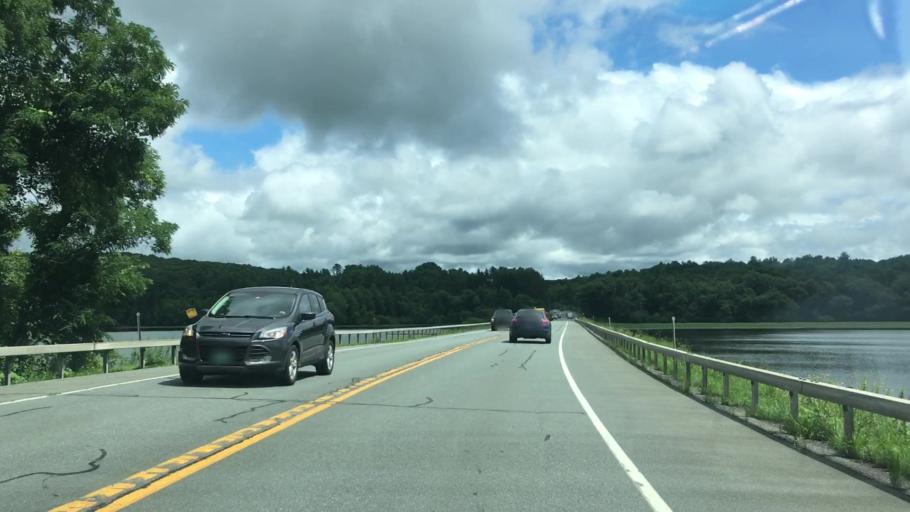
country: US
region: New York
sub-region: Rensselaer County
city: Poestenkill
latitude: 42.8192
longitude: -73.5227
